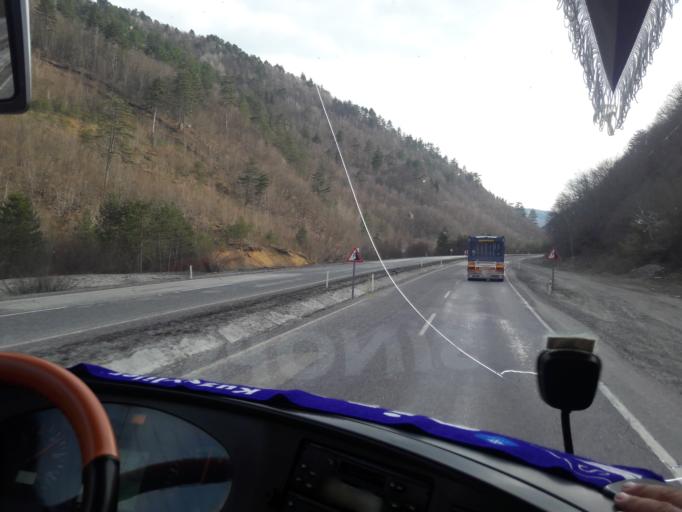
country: TR
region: Kastamonu
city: Kuzyaka
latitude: 41.1332
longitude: 33.7746
